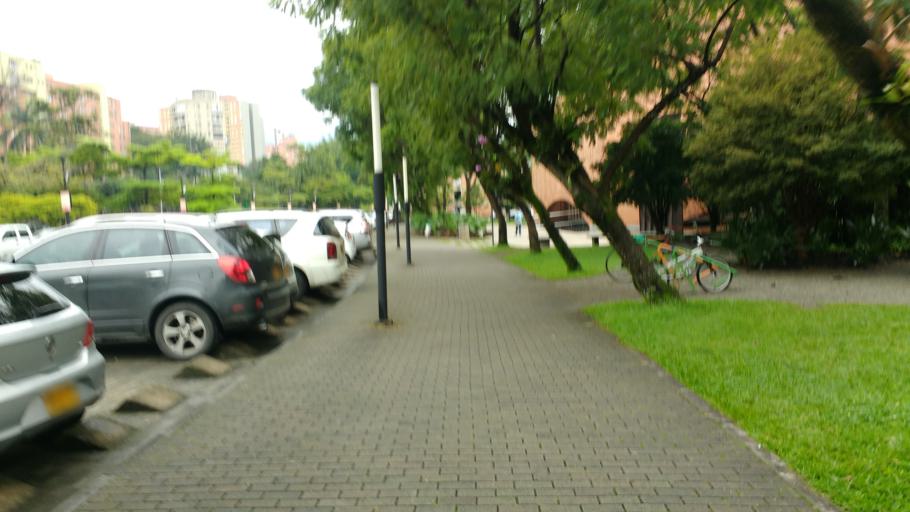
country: CO
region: Antioquia
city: Itagui
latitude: 6.2018
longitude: -75.5780
